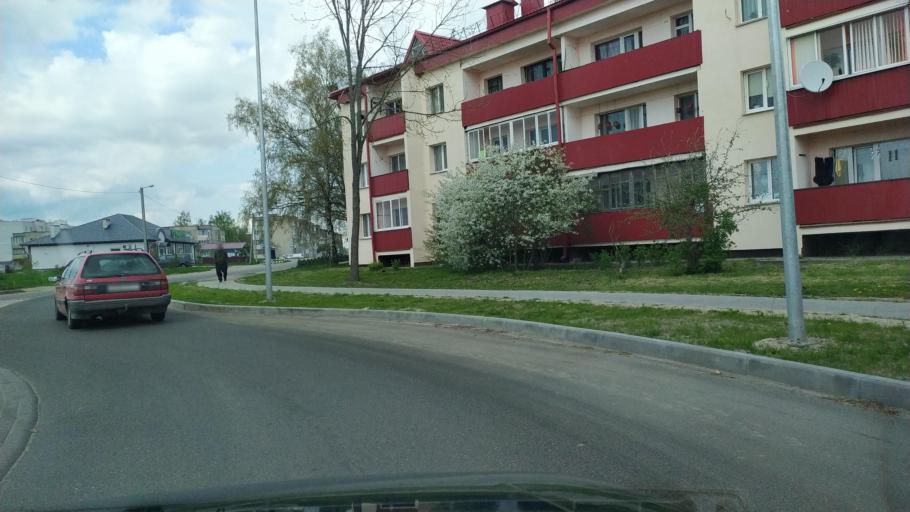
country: BY
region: Brest
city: Pruzhany
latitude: 52.5589
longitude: 24.4280
